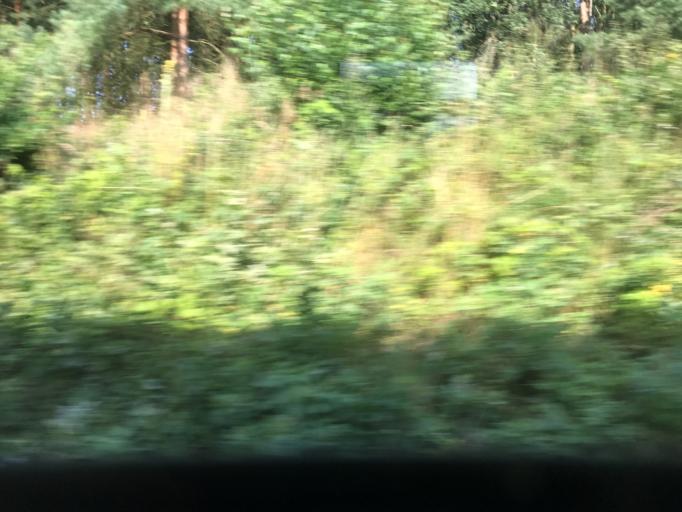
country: CZ
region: Jihocesky
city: Sobeslav
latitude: 49.2725
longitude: 14.7046
